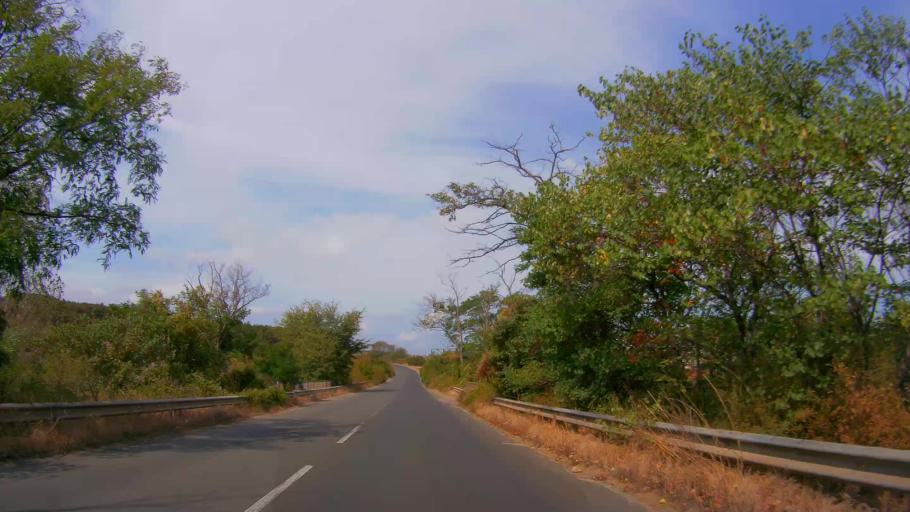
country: BG
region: Burgas
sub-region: Obshtina Sozopol
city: Sozopol
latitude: 42.4085
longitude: 27.6988
